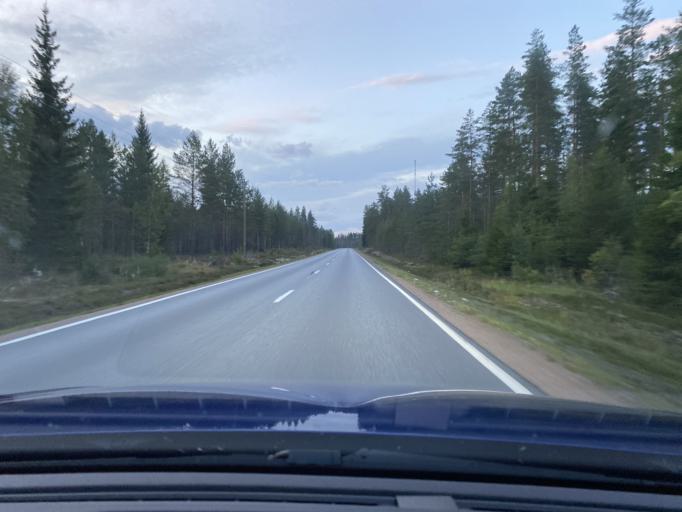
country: FI
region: Satakunta
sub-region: Pohjois-Satakunta
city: Honkajoki
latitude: 62.1877
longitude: 22.2956
